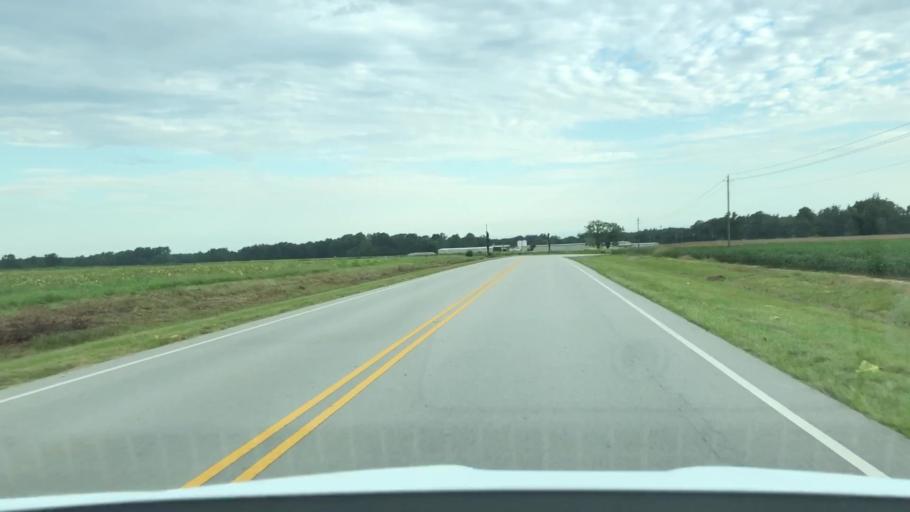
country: US
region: North Carolina
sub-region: Jones County
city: Trenton
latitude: 35.0505
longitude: -77.3544
